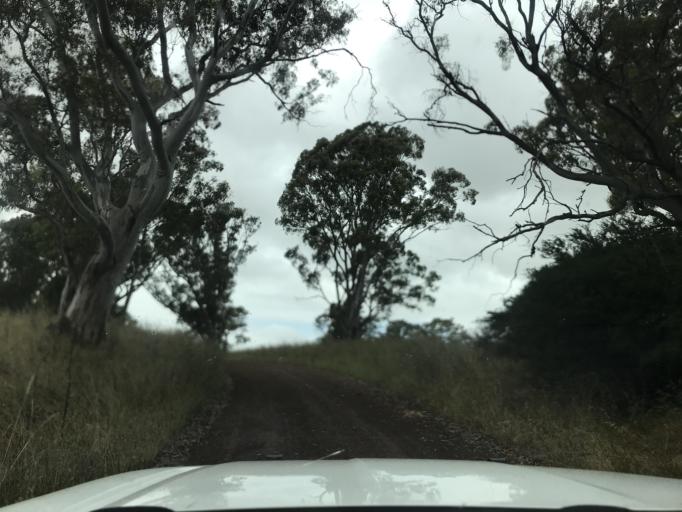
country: AU
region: South Australia
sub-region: Wattle Range
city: Penola
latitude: -37.2357
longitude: 141.4714
